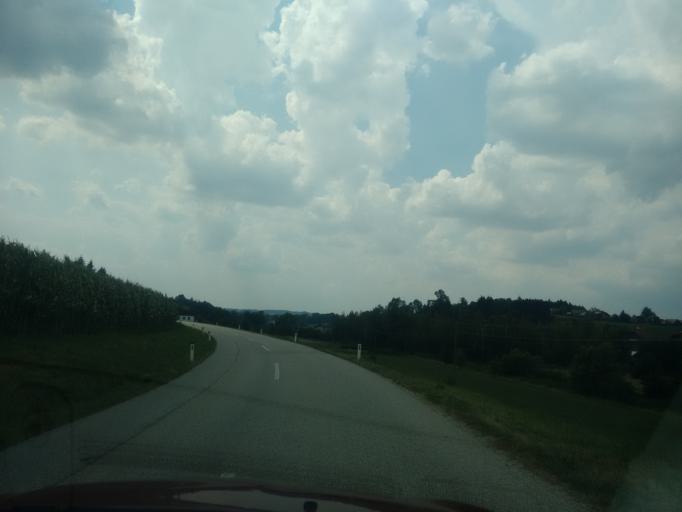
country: AT
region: Upper Austria
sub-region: Politischer Bezirk Grieskirchen
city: Bad Schallerbach
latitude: 48.2626
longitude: 13.9269
